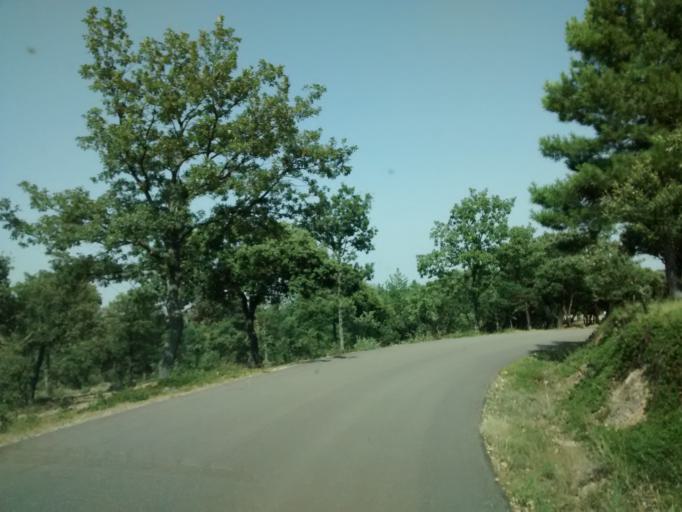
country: ES
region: Aragon
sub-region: Provincia de Zaragoza
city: Lituenigo
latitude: 41.8159
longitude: -1.7913
